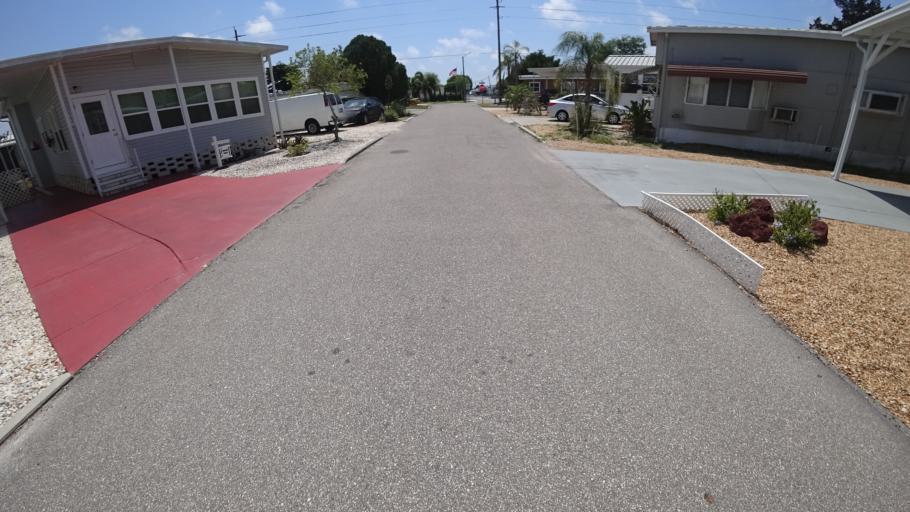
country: US
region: Florida
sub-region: Manatee County
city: Bayshore Gardens
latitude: 27.4233
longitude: -82.5844
